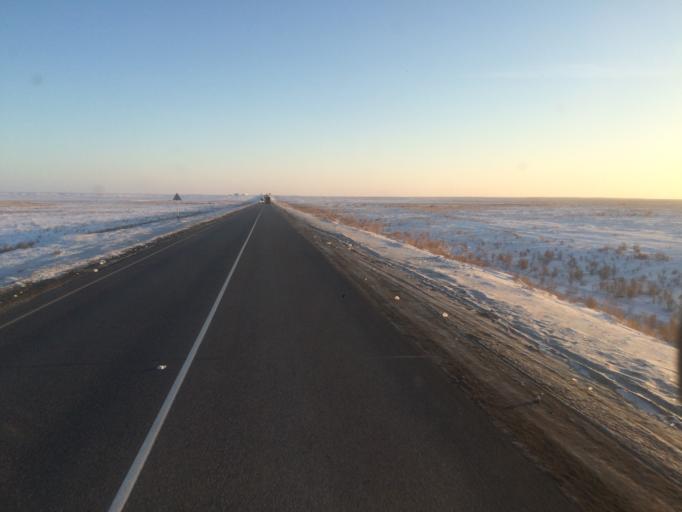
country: KZ
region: Qyzylorda
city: Sekseuil
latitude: 47.8171
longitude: 61.3403
